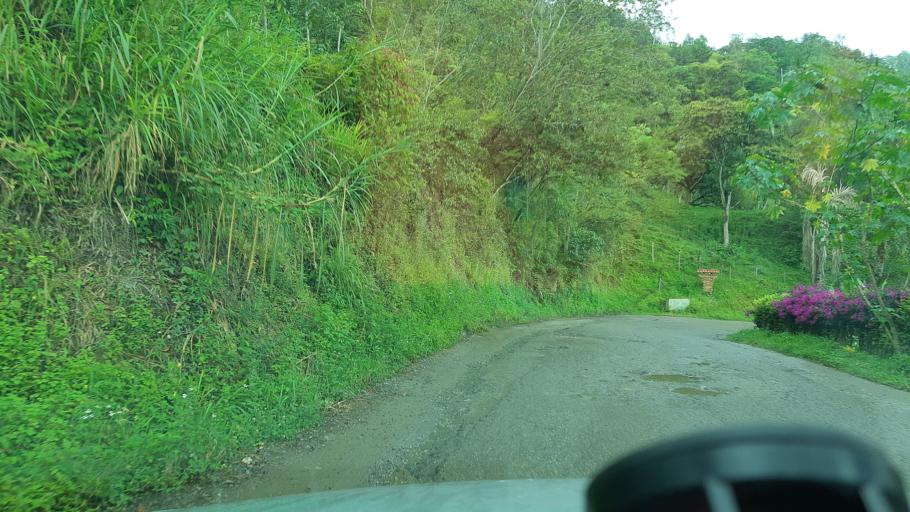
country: CO
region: Boyaca
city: Garagoa
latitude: 5.1241
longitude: -73.3626
